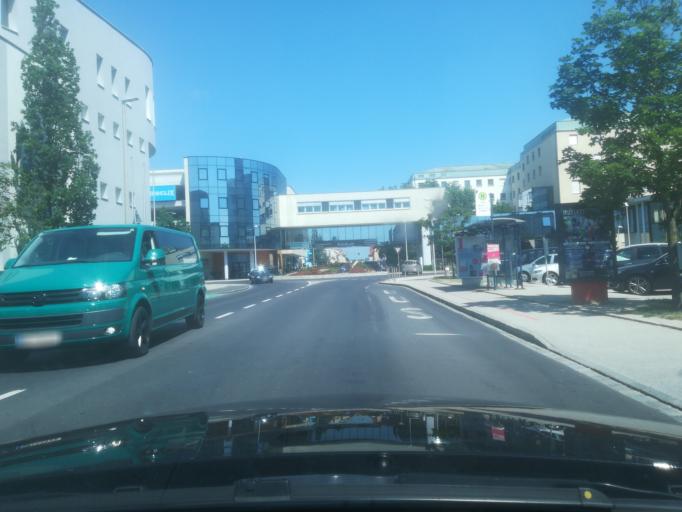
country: AT
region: Upper Austria
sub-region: Wels Stadt
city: Wels
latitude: 48.1725
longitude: 14.0233
